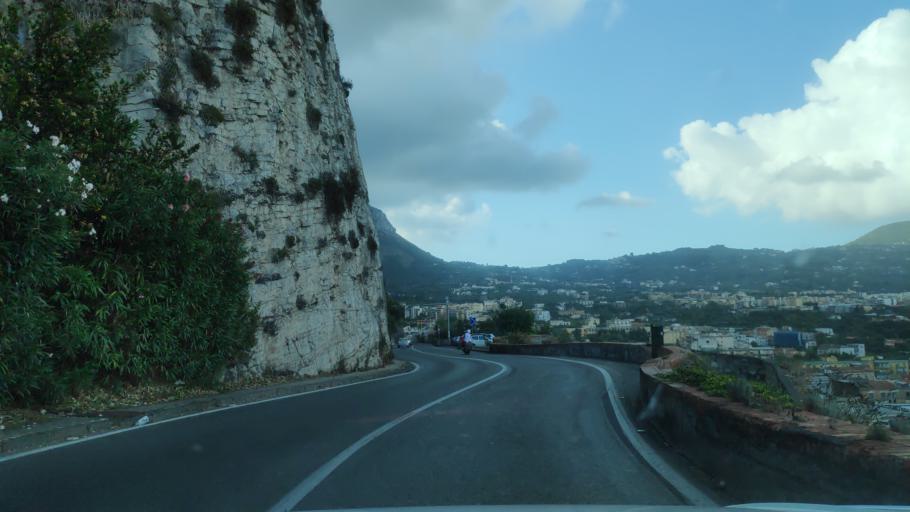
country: IT
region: Campania
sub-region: Provincia di Napoli
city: Meta
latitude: 40.6472
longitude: 14.4126
